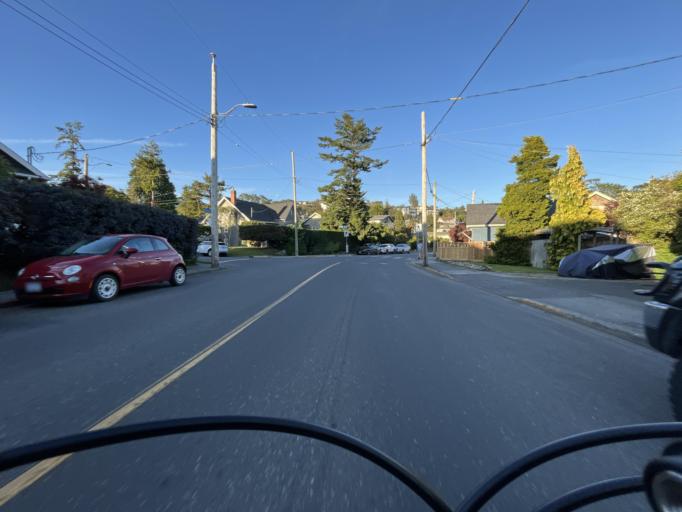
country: CA
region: British Columbia
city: Victoria
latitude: 48.4122
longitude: -123.3291
